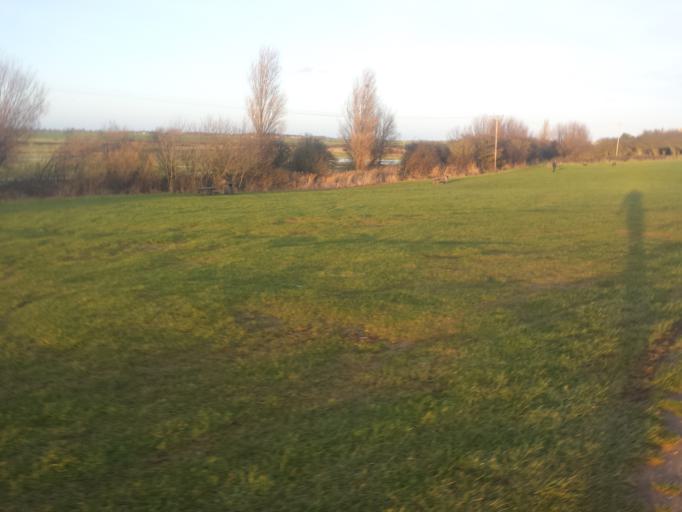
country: GB
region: England
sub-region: Essex
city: Frinton-on-Sea
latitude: 51.8079
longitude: 1.2099
